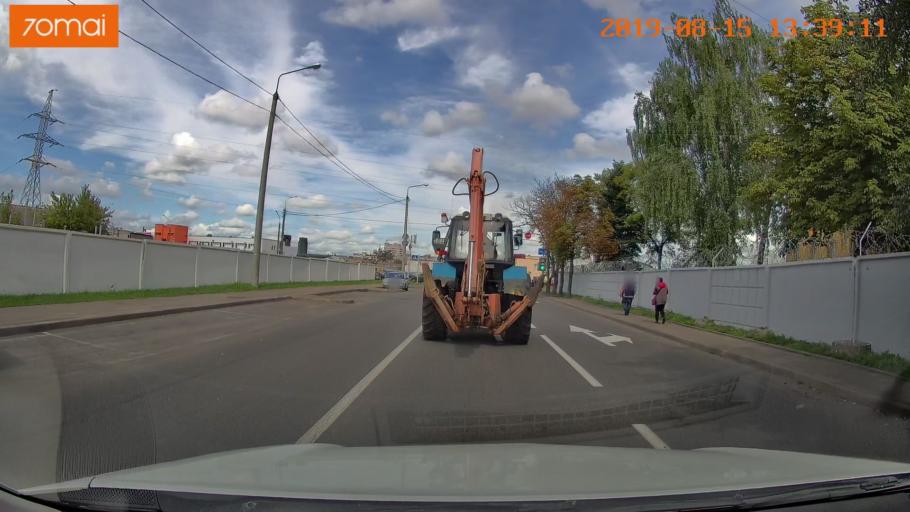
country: BY
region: Minsk
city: Minsk
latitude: 53.8767
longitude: 27.5933
